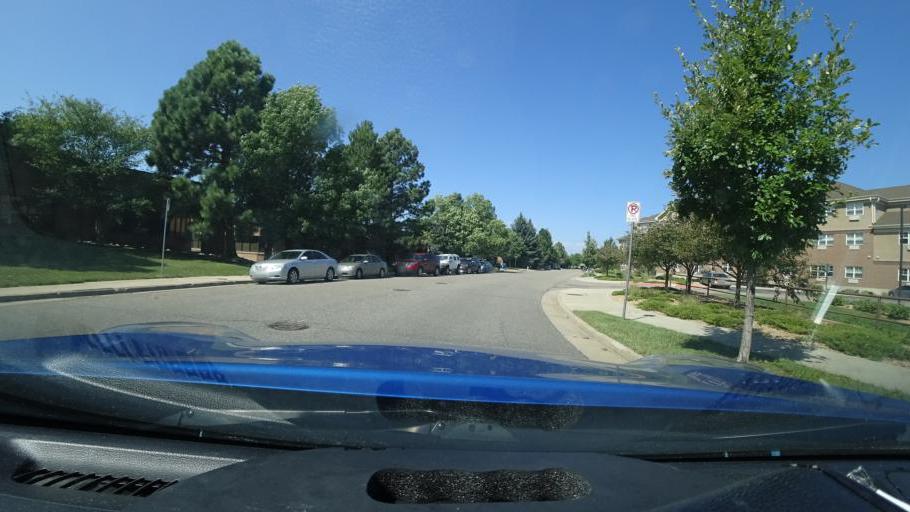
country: US
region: Colorado
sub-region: Adams County
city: Aurora
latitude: 39.6781
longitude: -104.8210
